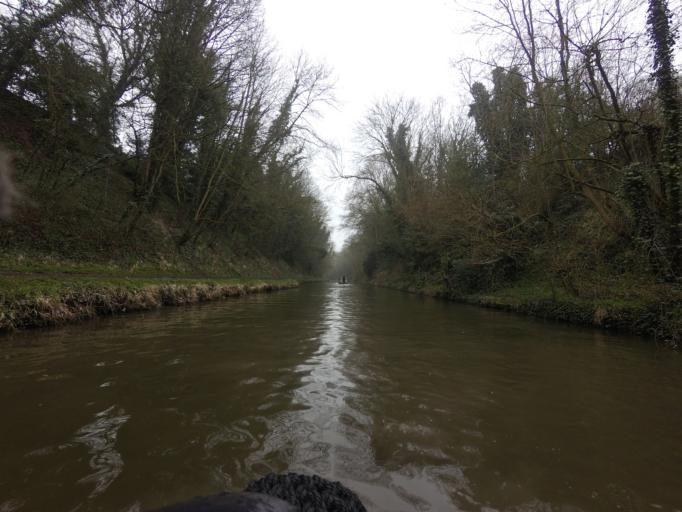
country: GB
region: England
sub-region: Hertfordshire
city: Tring
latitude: 51.8033
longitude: -0.6355
